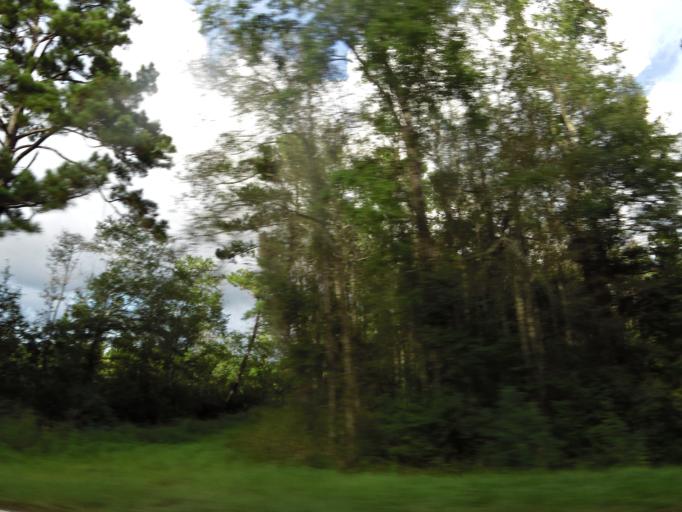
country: US
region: Georgia
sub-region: Liberty County
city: Midway
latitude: 31.8640
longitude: -81.4351
